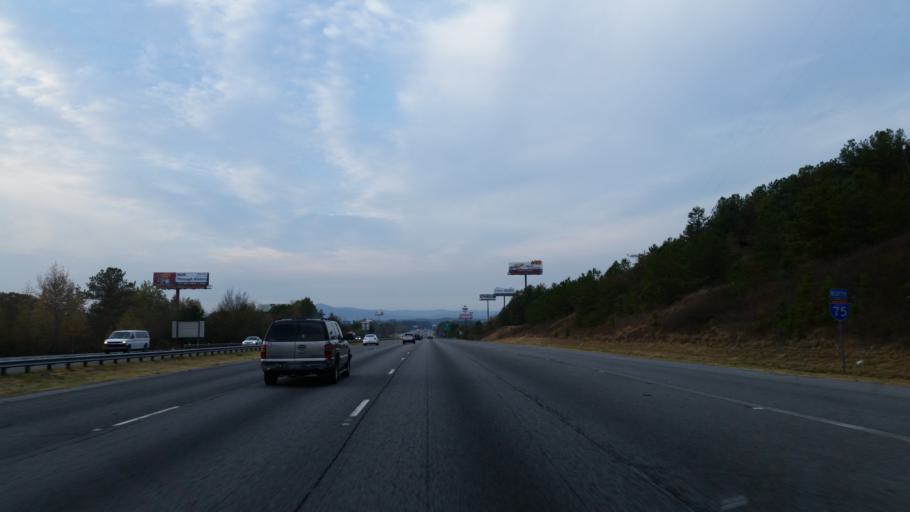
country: US
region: Georgia
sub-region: Gordon County
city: Calhoun
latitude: 34.5462
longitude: -84.9254
